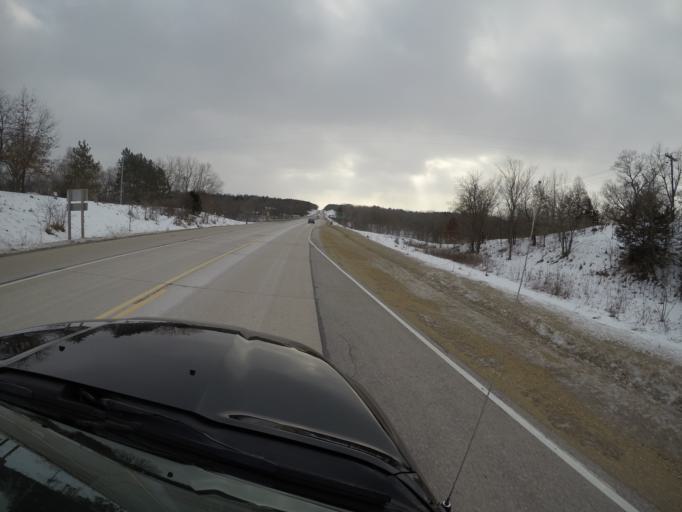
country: US
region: Wisconsin
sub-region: Trempealeau County
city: Galesville
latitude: 44.0640
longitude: -91.2911
